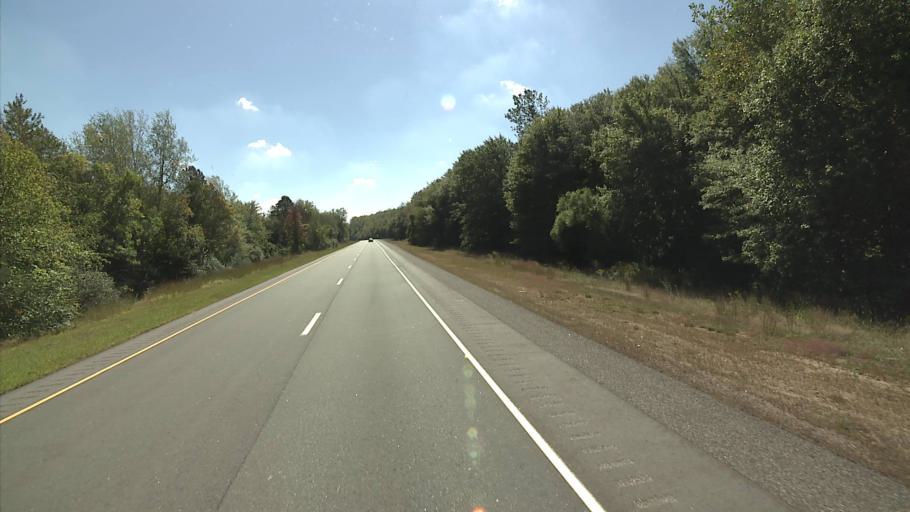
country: US
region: Connecticut
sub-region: New London County
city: Colchester
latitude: 41.4932
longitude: -72.3020
